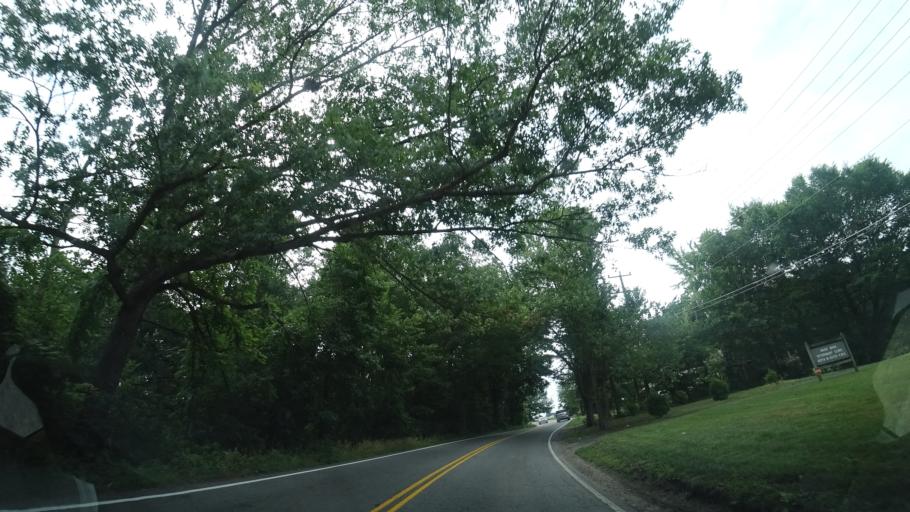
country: US
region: Virginia
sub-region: City of Fredericksburg
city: Fredericksburg
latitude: 38.2503
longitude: -77.5048
